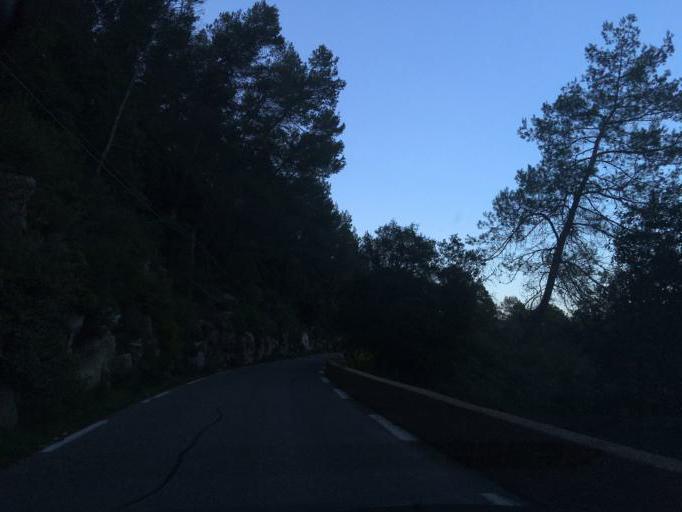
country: FR
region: Provence-Alpes-Cote d'Azur
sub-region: Departement du Var
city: Salernes
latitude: 43.5232
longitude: 6.2385
